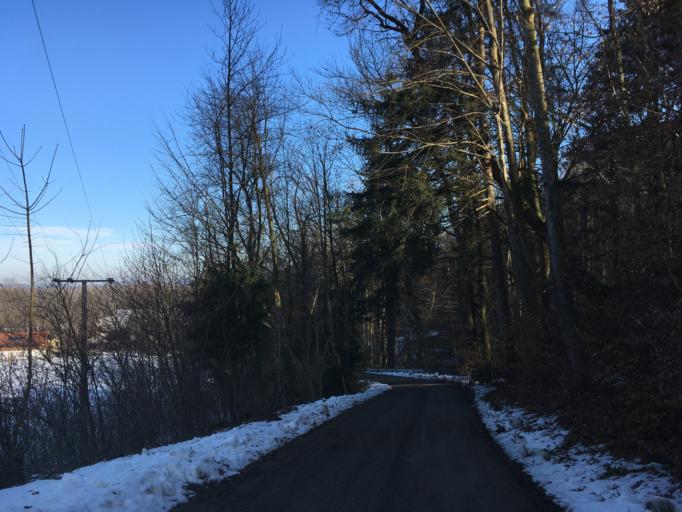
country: DE
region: Bavaria
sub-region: Upper Bavaria
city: Schechen
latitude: 47.9184
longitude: 12.1478
